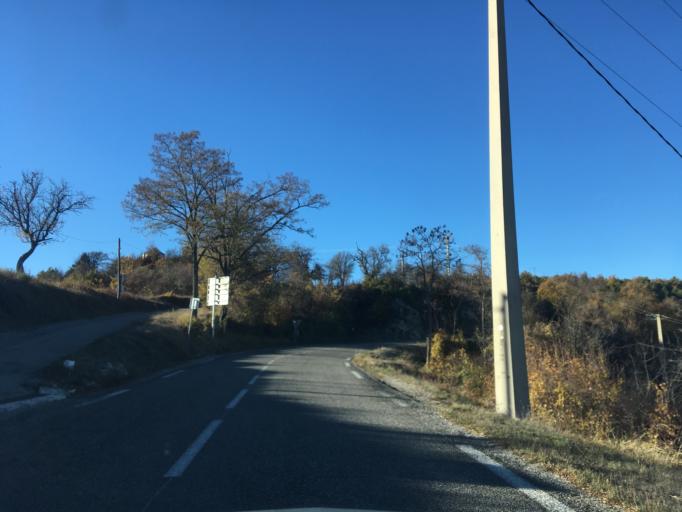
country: FR
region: Provence-Alpes-Cote d'Azur
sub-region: Departement du Var
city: Bargemon
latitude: 43.7131
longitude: 6.5047
